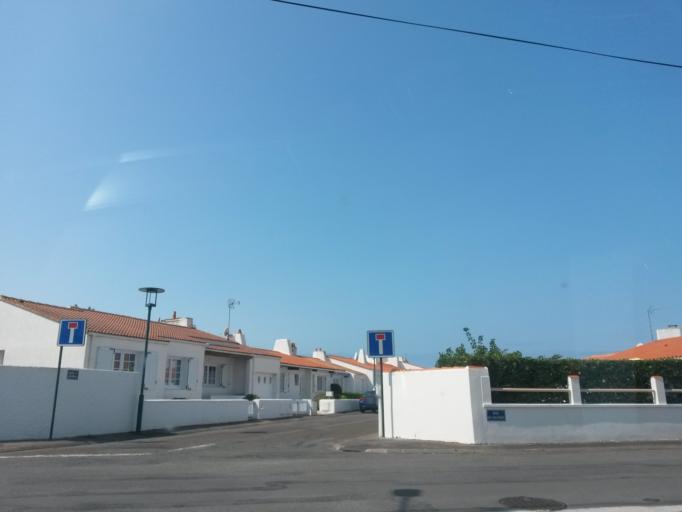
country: FR
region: Pays de la Loire
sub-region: Departement de la Vendee
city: Les Sables-d'Olonne
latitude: 46.4913
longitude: -1.7991
